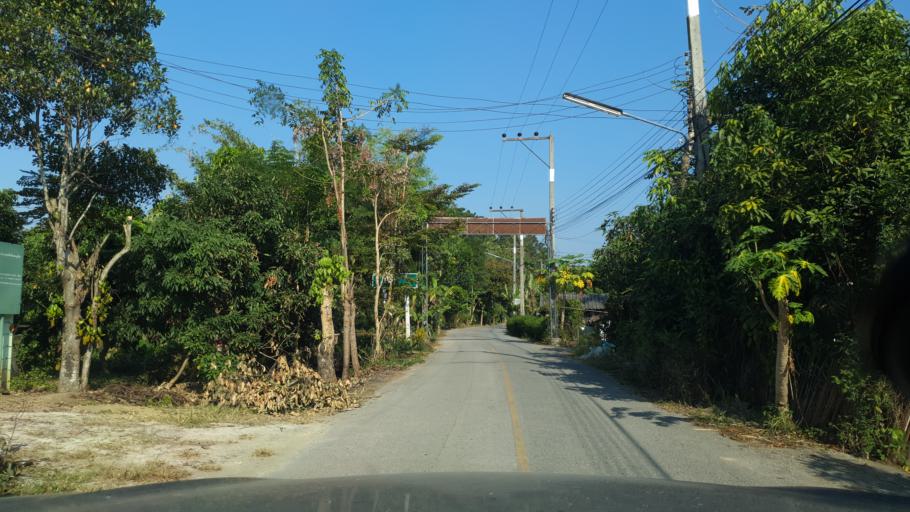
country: TH
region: Chiang Mai
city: Saraphi
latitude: 18.7124
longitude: 99.0736
